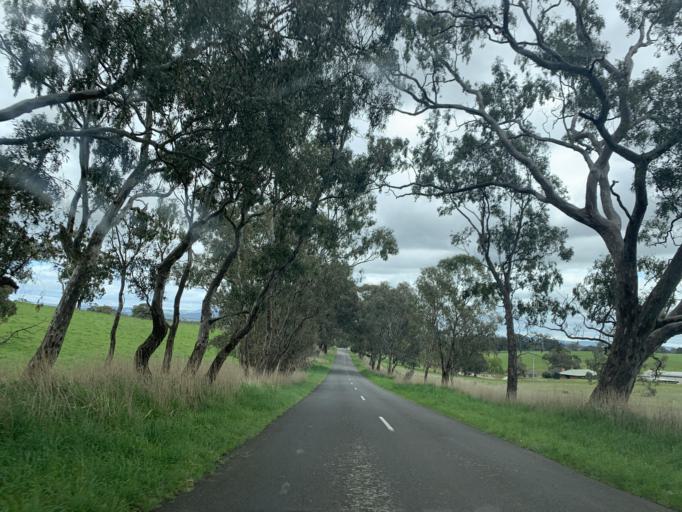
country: AU
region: Victoria
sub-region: Whittlesea
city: Whittlesea
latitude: -37.1859
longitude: 145.0225
